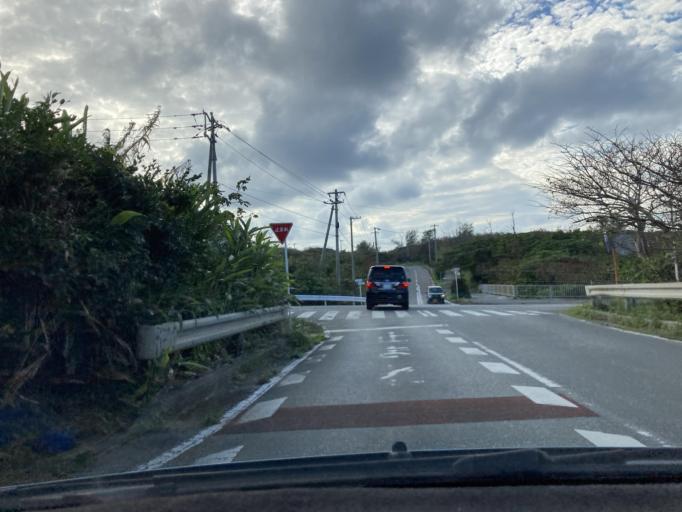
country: JP
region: Okinawa
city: Nago
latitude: 26.8665
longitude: 128.2573
